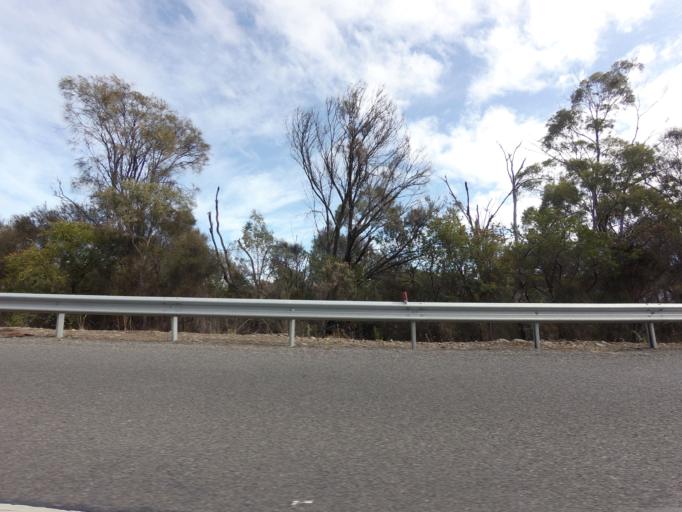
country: AU
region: Tasmania
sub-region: Clarence
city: Sandford
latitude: -43.1092
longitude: 147.7458
